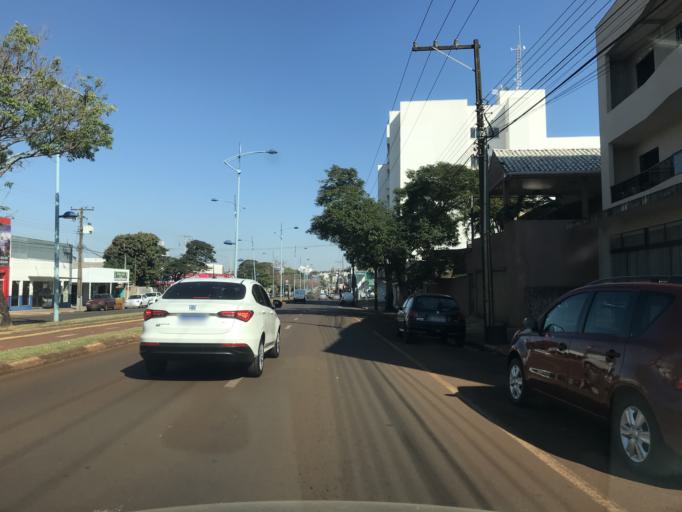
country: BR
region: Parana
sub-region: Toledo
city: Toledo
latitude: -24.7254
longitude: -53.7263
